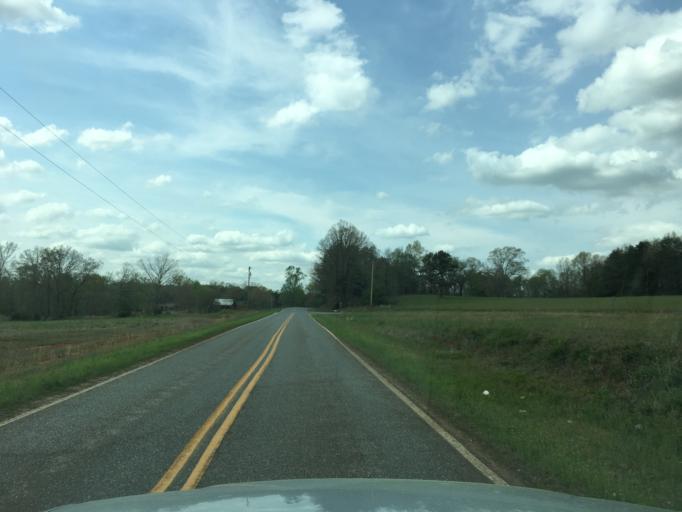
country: US
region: North Carolina
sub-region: Rutherford County
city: Spindale
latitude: 35.2334
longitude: -81.9684
